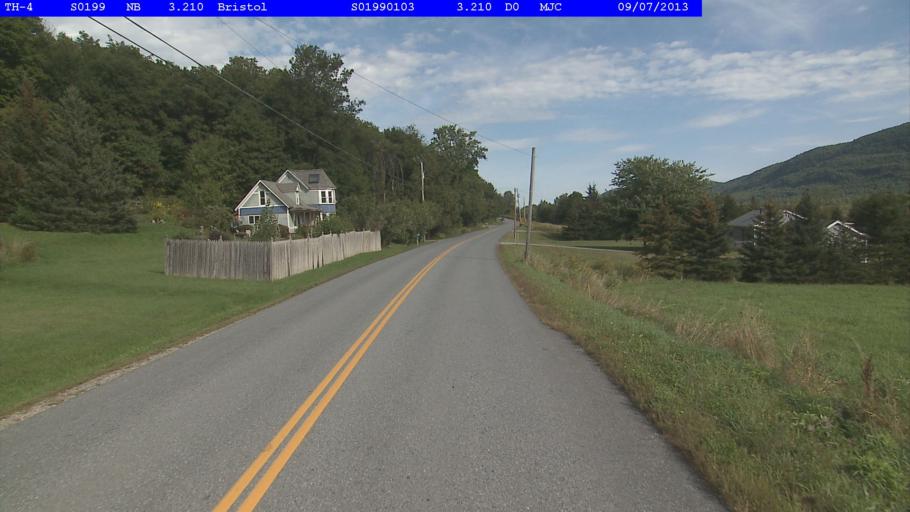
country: US
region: Vermont
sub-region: Addison County
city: Bristol
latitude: 44.1744
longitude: -73.1022
